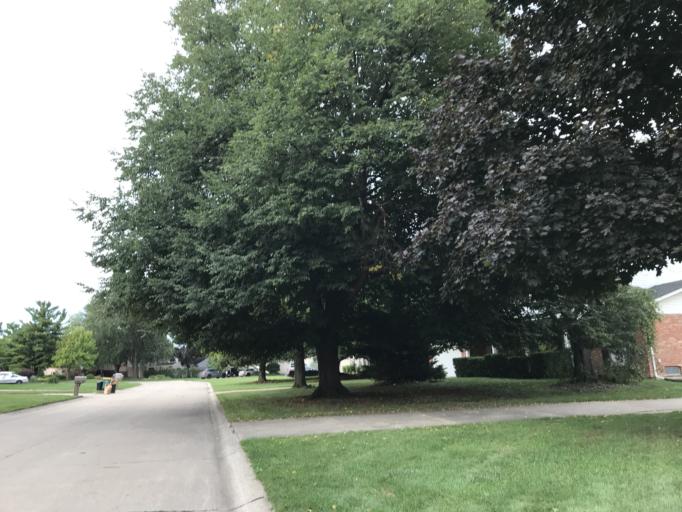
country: US
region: Michigan
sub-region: Oakland County
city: Franklin
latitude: 42.4825
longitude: -83.3267
